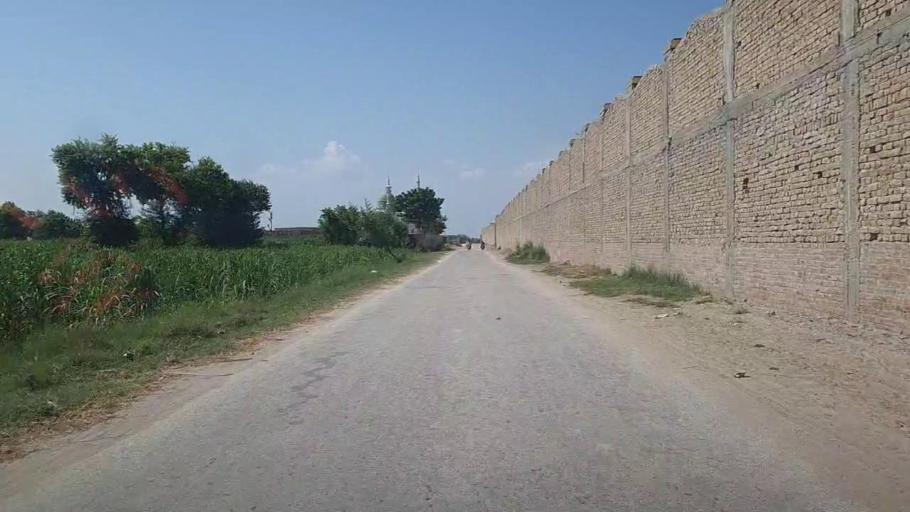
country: PK
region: Sindh
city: Khairpur
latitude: 28.0645
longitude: 69.6450
